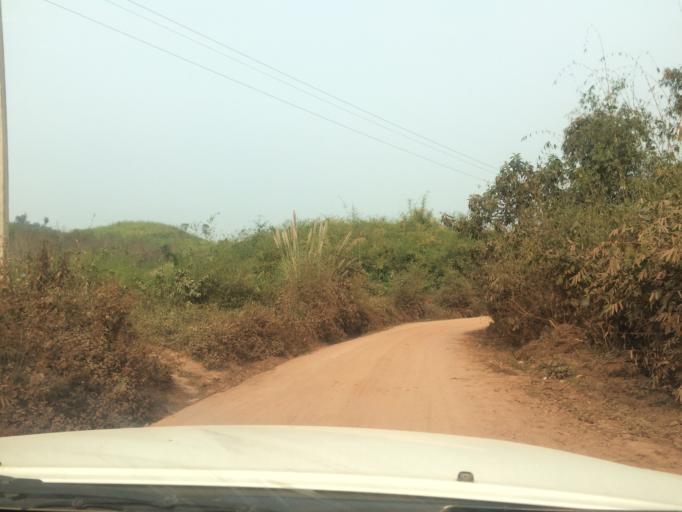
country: LA
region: Loungnamtha
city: Muang Nale
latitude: 20.4187
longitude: 101.6798
